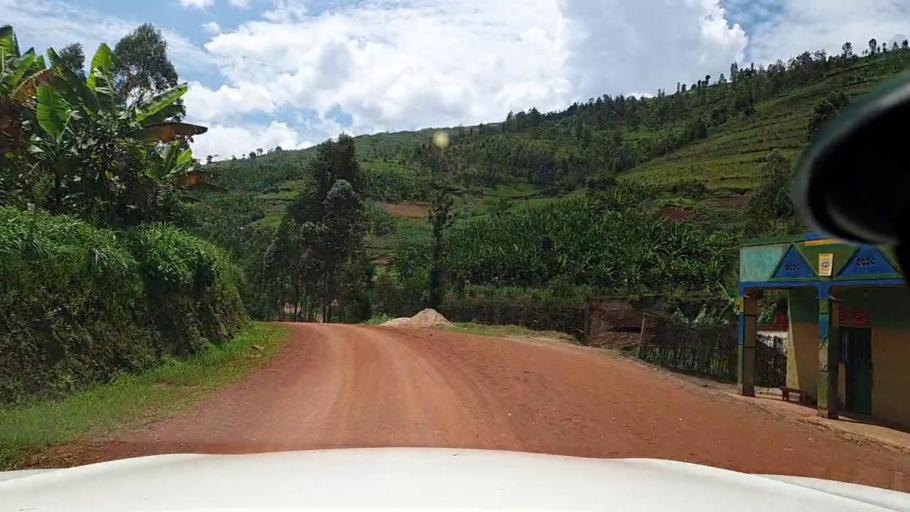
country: RW
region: Northern Province
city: Musanze
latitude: -1.6940
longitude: 29.8210
